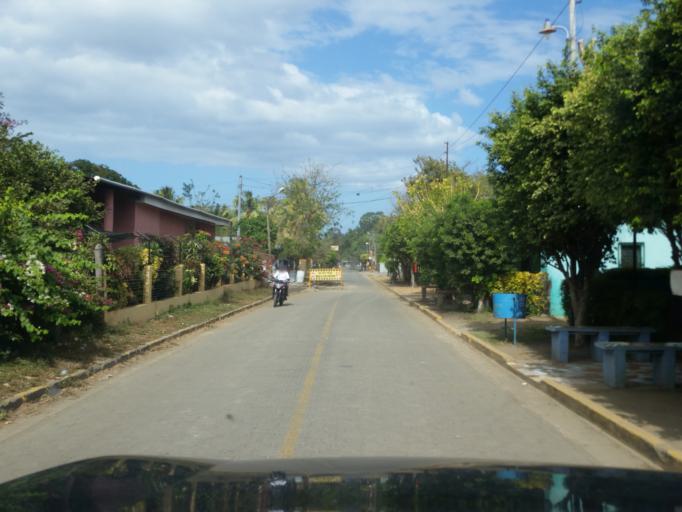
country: NI
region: Rivas
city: Potosi
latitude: 11.4924
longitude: -85.8571
